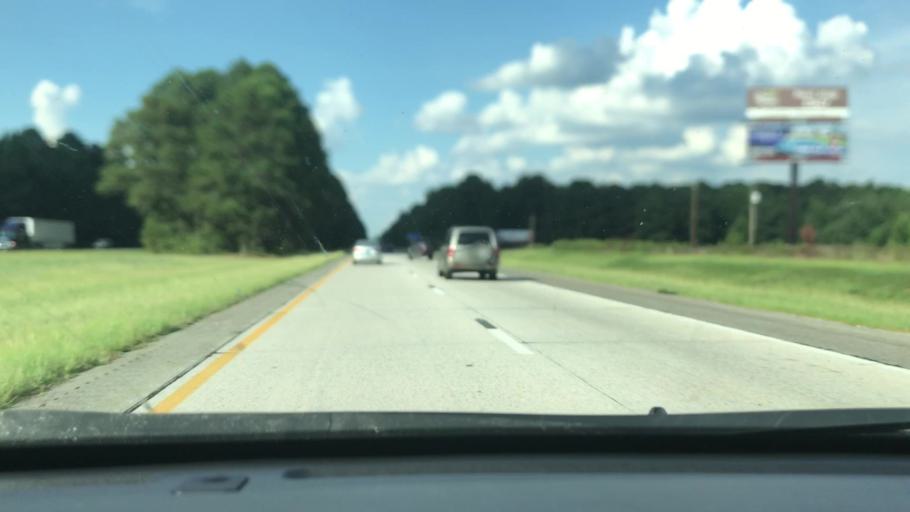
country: US
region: South Carolina
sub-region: Florence County
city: Timmonsville
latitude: 34.1030
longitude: -79.9200
